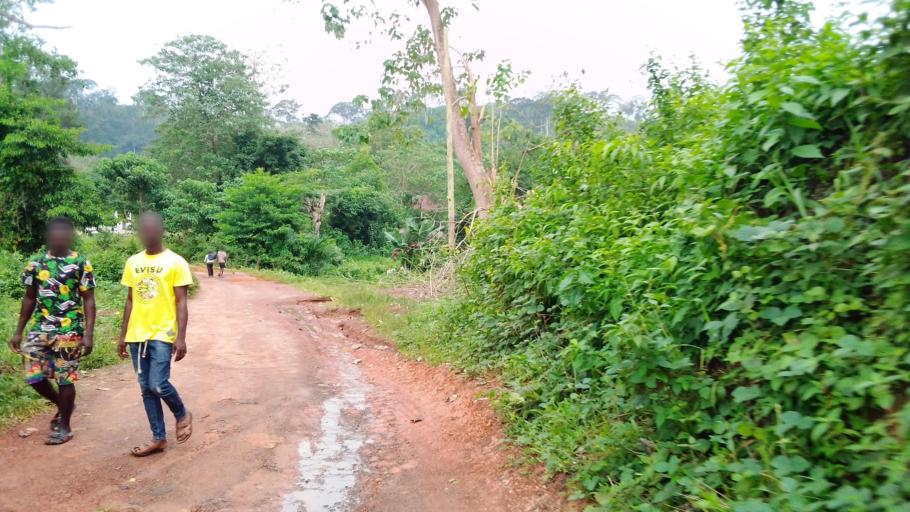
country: SL
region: Eastern Province
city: Kenema
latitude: 7.8886
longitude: -11.1954
